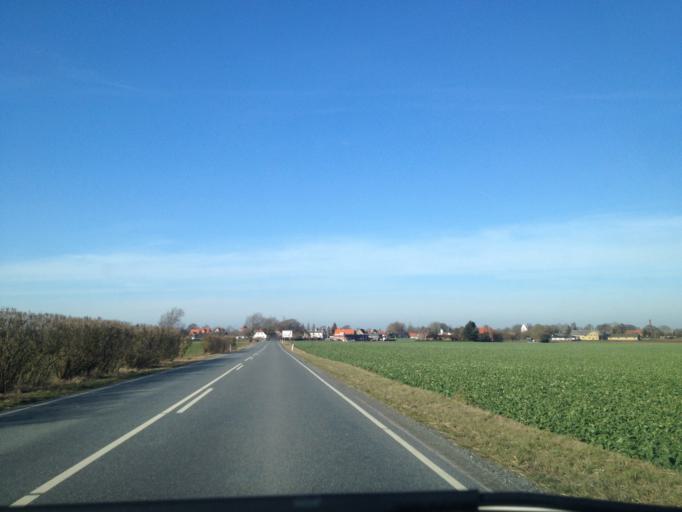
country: DK
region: South Denmark
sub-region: Kerteminde Kommune
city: Kerteminde
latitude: 55.4940
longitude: 10.6539
